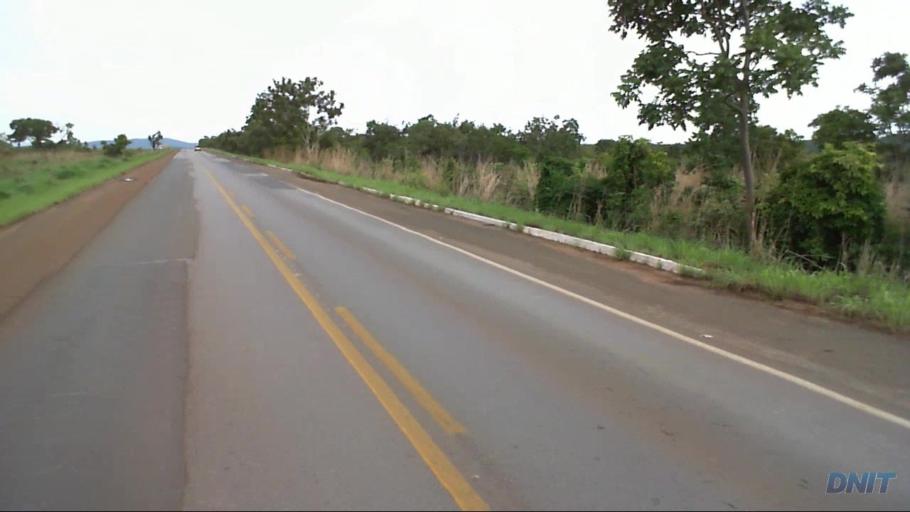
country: BR
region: Goias
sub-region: Barro Alto
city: Barro Alto
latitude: -14.8638
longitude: -49.0175
